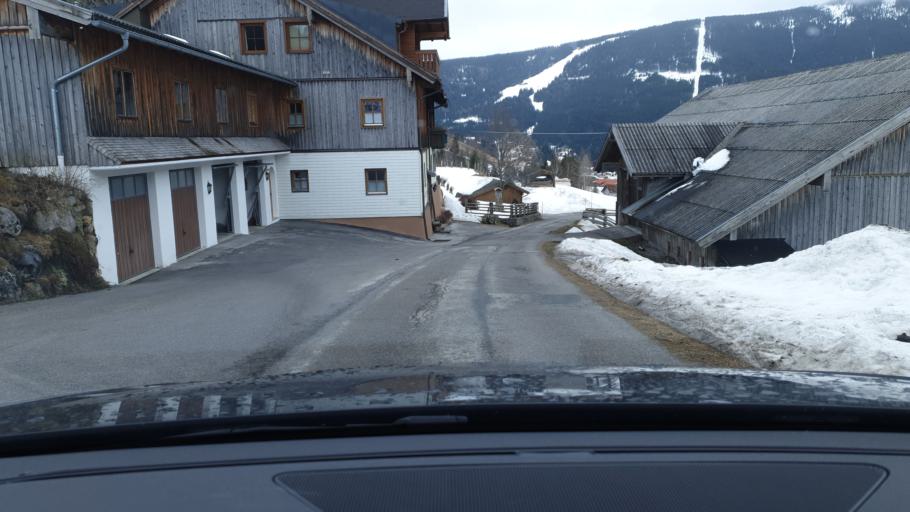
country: AT
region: Salzburg
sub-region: Politischer Bezirk Sankt Johann im Pongau
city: Filzmoos
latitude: 47.4479
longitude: 13.5224
